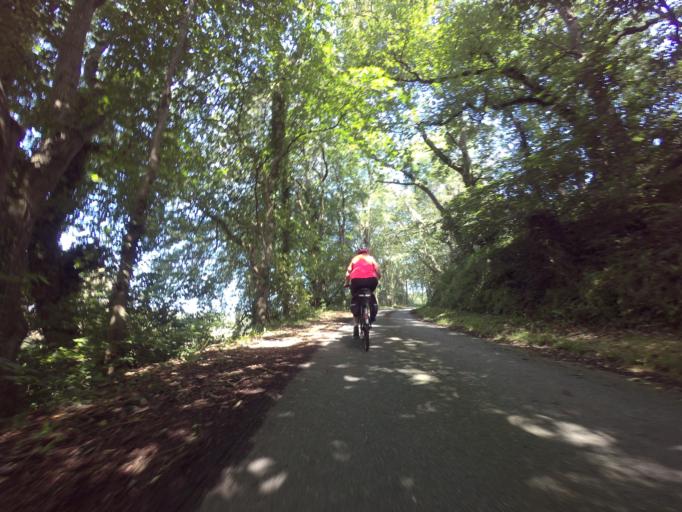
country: GB
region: Scotland
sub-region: Aberdeenshire
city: Banff
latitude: 57.6119
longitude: -2.5117
